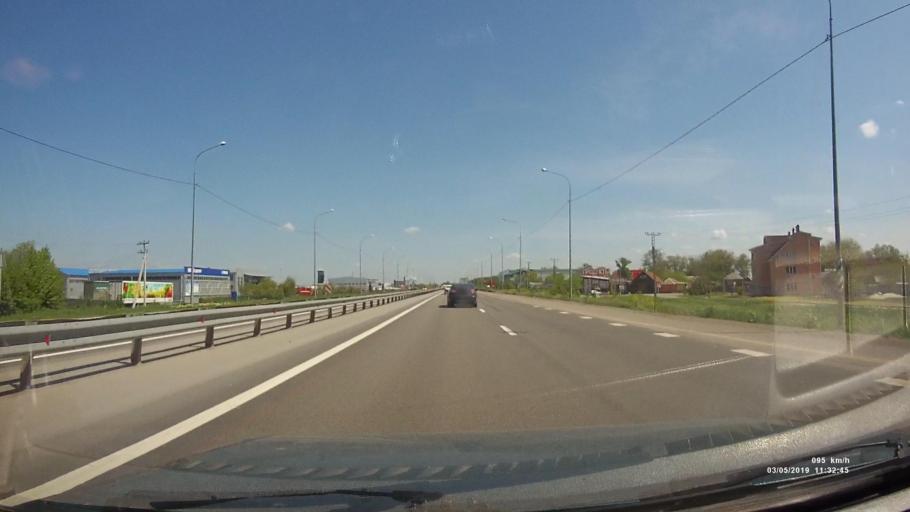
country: RU
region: Rostov
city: Bataysk
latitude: 47.1186
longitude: 39.8577
